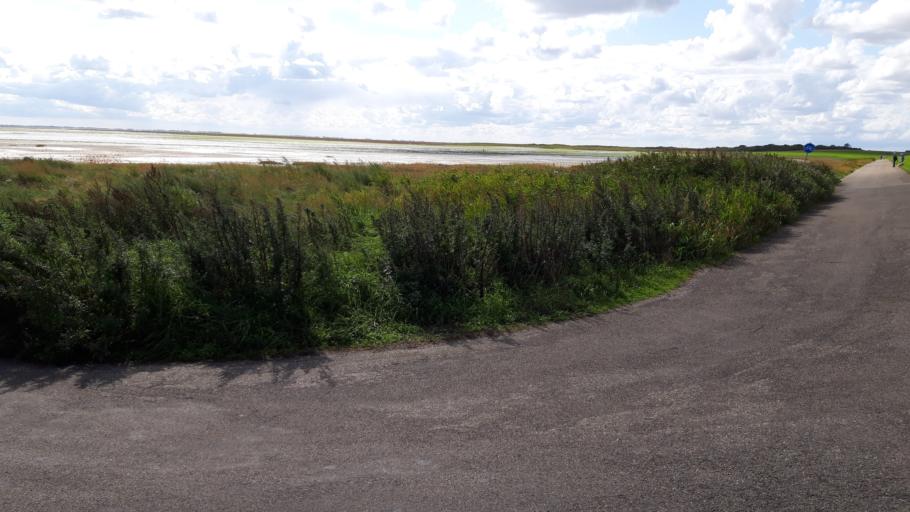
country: NL
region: Friesland
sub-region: Gemeente Schiermonnikoog
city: Schiermonnikoog
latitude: 53.4724
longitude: 6.1661
